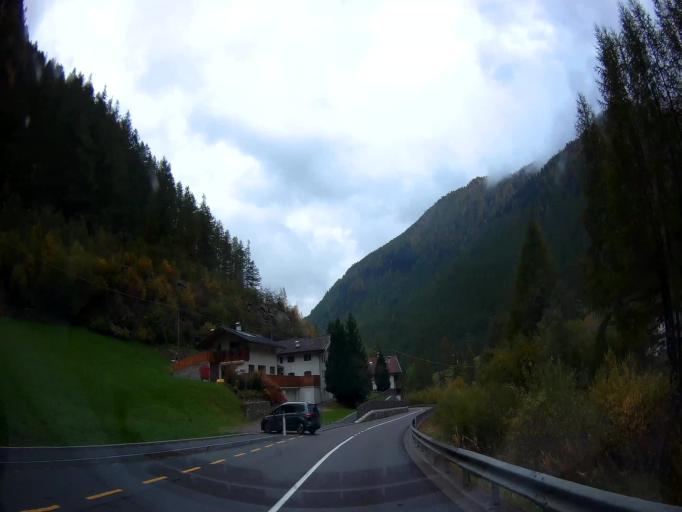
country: IT
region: Trentino-Alto Adige
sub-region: Bolzano
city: Senales
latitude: 46.7169
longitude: 10.8711
